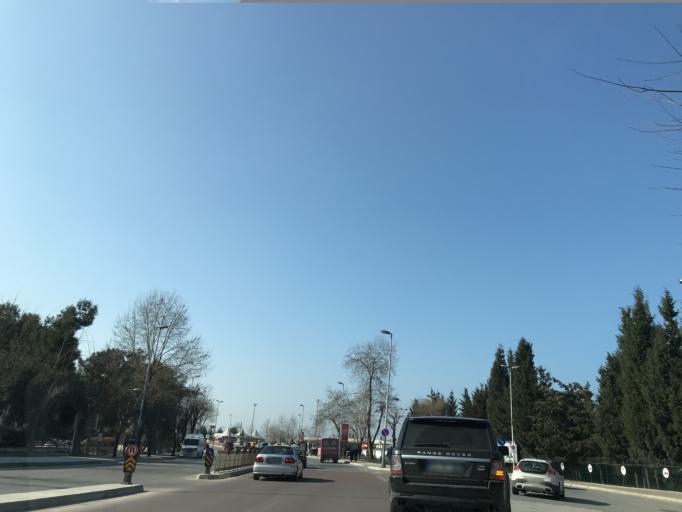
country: TR
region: Yalova
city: Yalova
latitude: 40.6586
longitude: 29.2811
